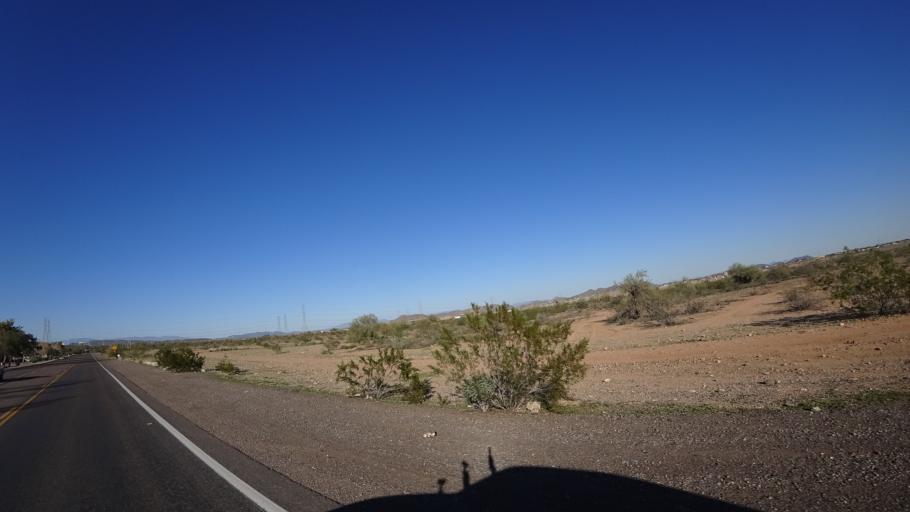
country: US
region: Arizona
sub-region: Maricopa County
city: Sun City West
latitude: 33.7003
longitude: -112.3123
